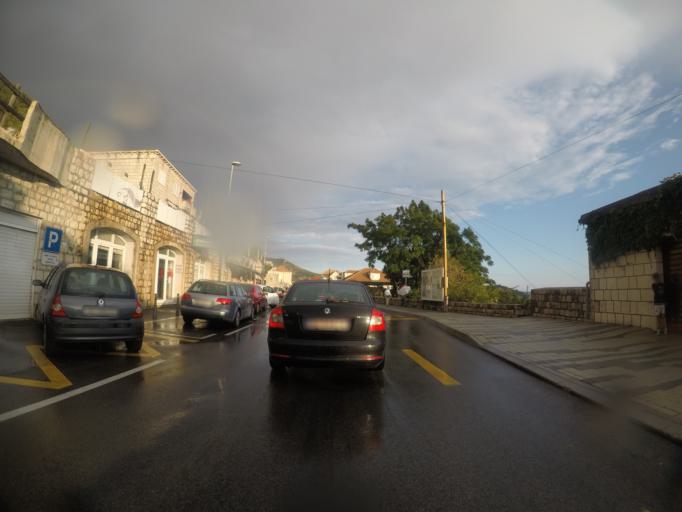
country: HR
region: Dubrovacko-Neretvanska
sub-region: Grad Dubrovnik
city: Dubrovnik
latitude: 42.6448
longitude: 18.1048
